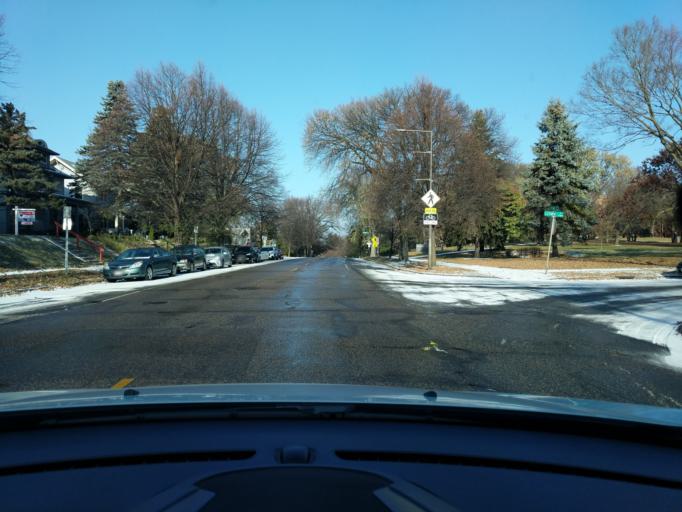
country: US
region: Minnesota
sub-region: Ramsey County
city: Lauderdale
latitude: 44.9828
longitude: -93.1960
